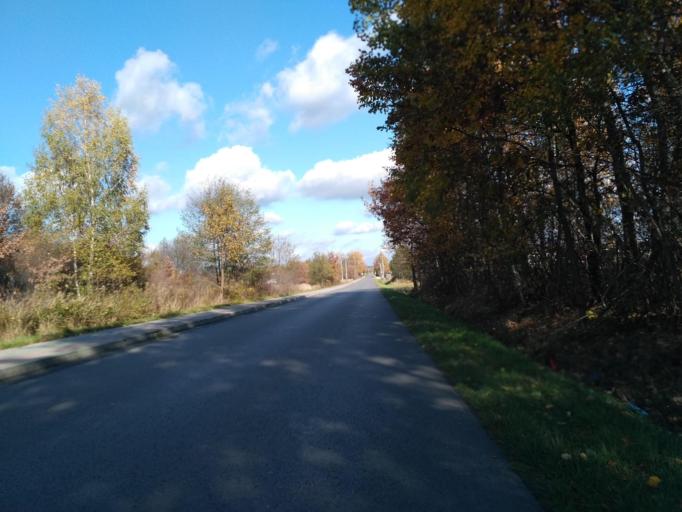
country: PL
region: Subcarpathian Voivodeship
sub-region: Powiat rzeszowski
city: Swilcza
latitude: 50.1172
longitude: 21.8992
